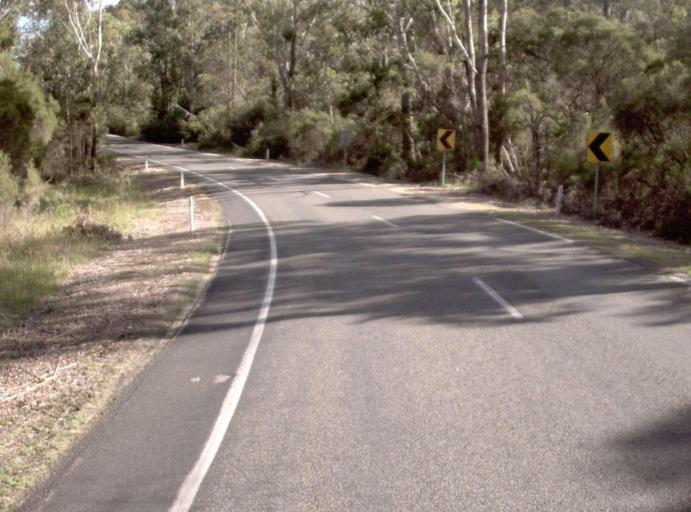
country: AU
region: Victoria
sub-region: East Gippsland
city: Lakes Entrance
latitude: -37.5494
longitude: 148.1484
